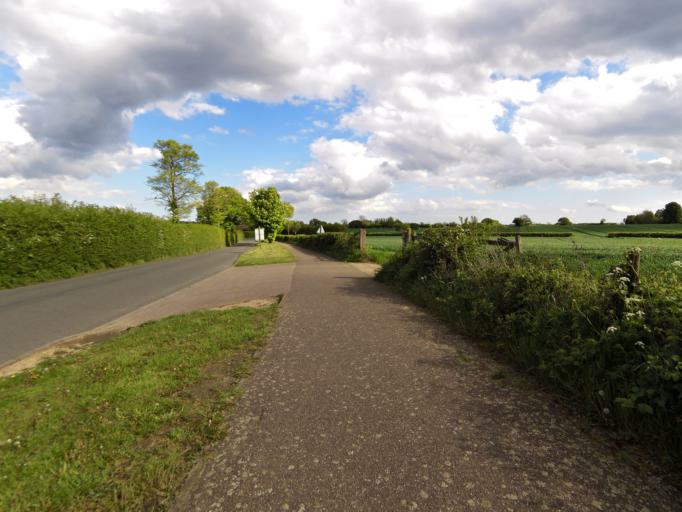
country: GB
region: England
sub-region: Suffolk
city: Woolpit
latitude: 52.2211
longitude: 0.8960
